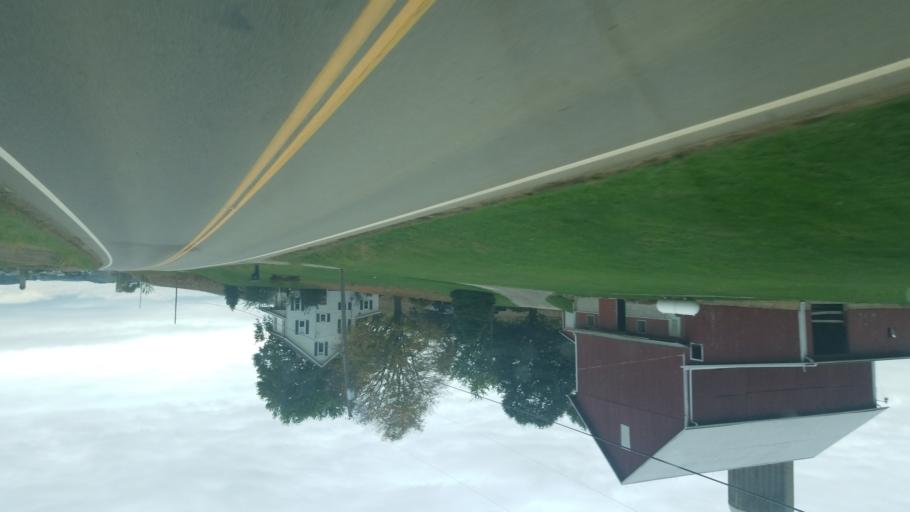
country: US
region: Ohio
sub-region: Ashland County
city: Loudonville
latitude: 40.6530
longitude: -82.2691
